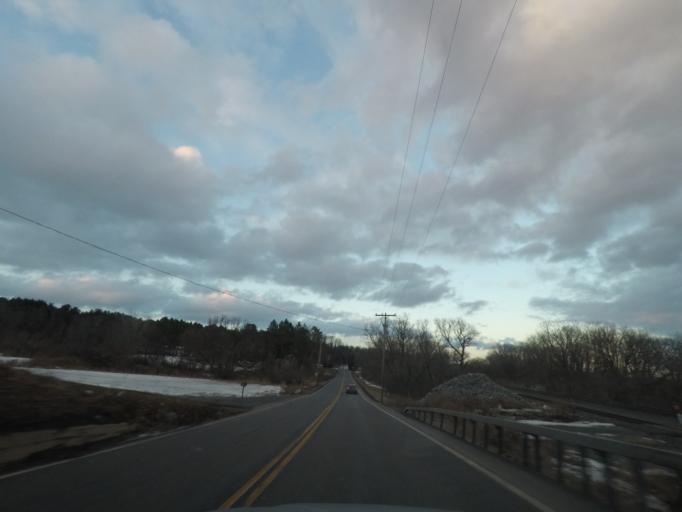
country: US
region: New York
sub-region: Montgomery County
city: Fonda
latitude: 42.9480
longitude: -74.3948
